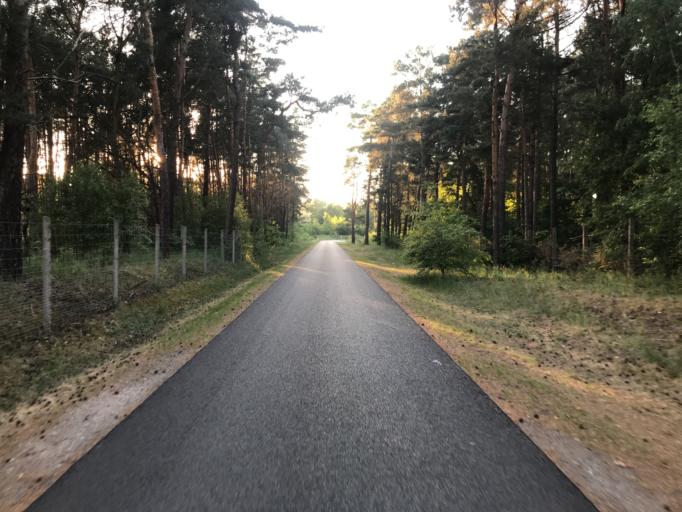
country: DE
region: Brandenburg
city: Melchow
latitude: 52.8319
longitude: 13.6742
